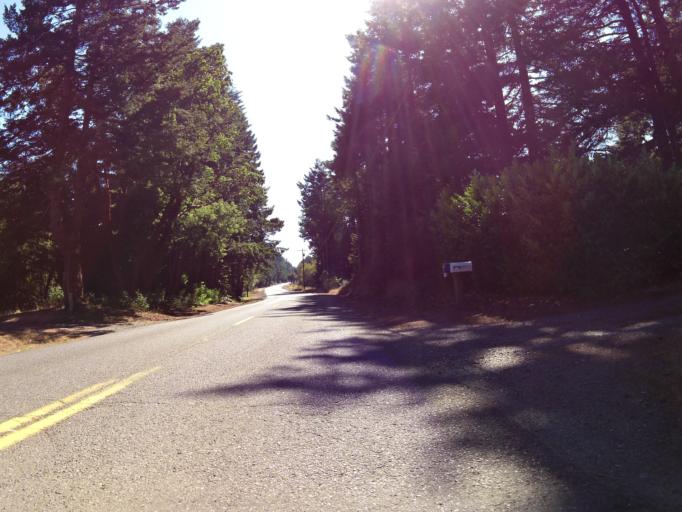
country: US
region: Oregon
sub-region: Coos County
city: Bandon
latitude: 43.1796
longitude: -124.3704
